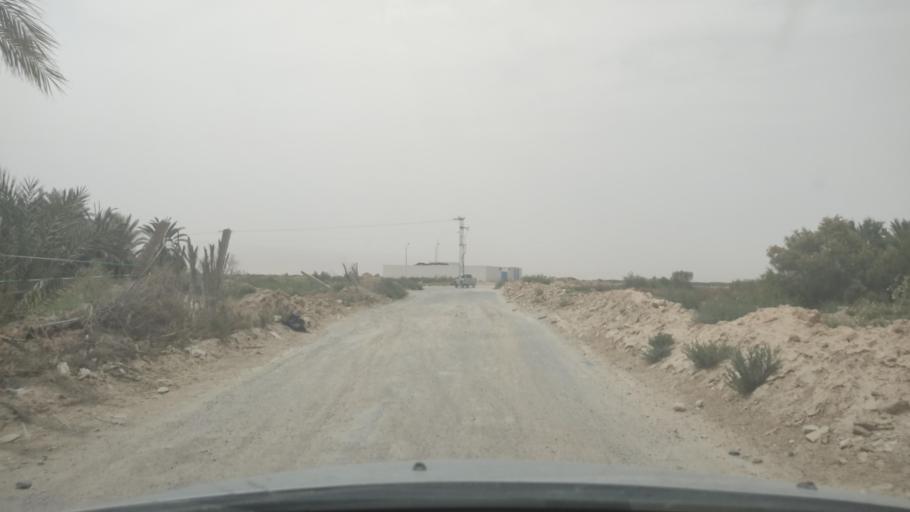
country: TN
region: Gafsa
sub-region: Gafsa Municipality
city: Gafsa
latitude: 34.3261
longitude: 8.9515
